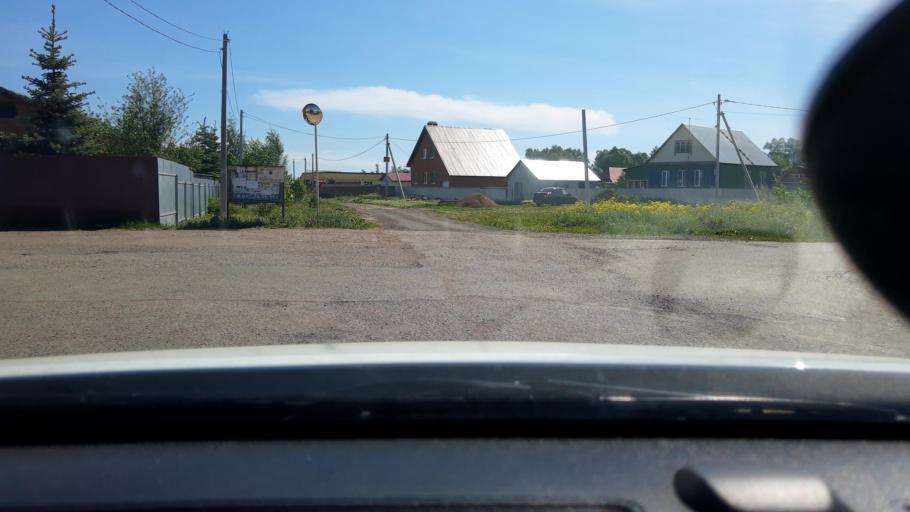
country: RU
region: Bashkortostan
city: Avdon
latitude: 54.5056
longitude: 55.8151
